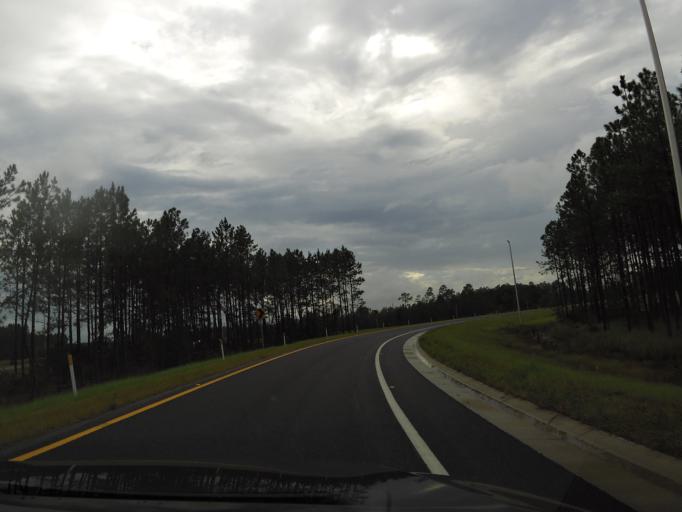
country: US
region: Florida
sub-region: Duval County
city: Baldwin
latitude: 30.3040
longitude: -81.8753
